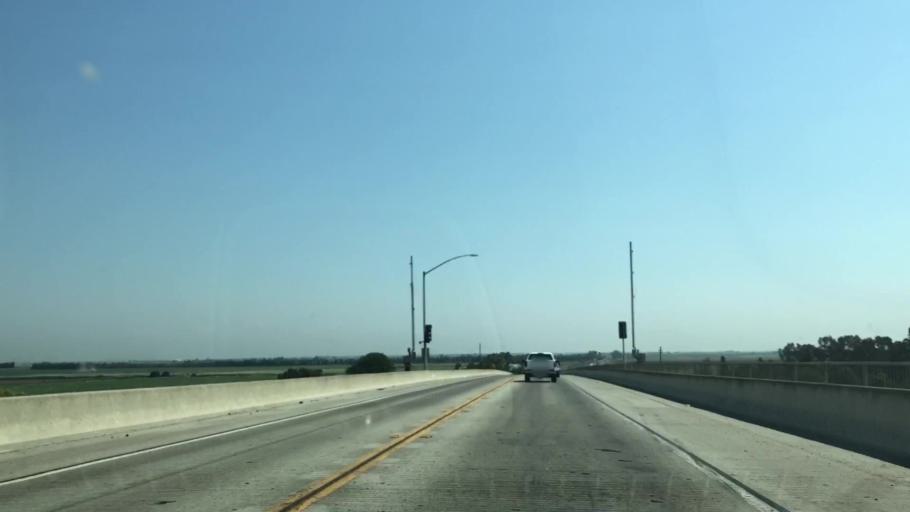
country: US
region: California
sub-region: Sacramento County
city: Walnut Grove
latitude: 38.1151
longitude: -121.4968
